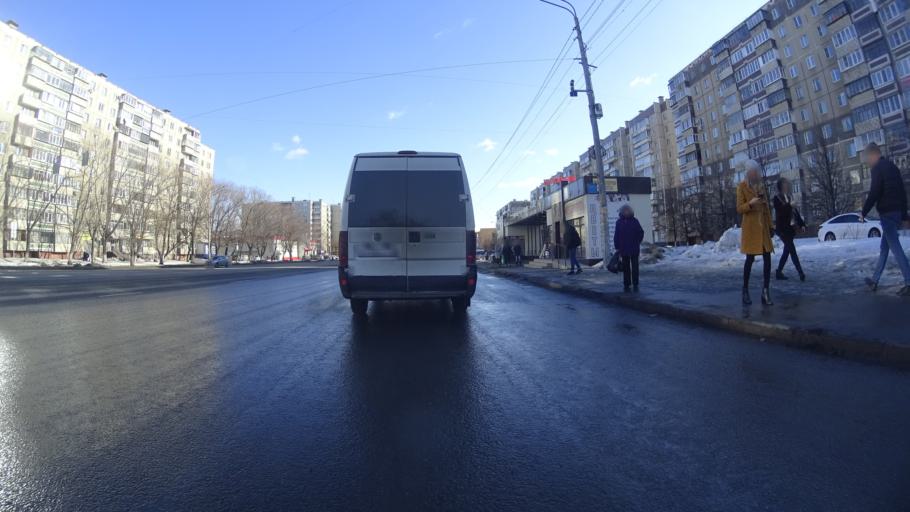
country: RU
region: Chelyabinsk
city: Roshchino
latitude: 55.1904
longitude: 61.2812
